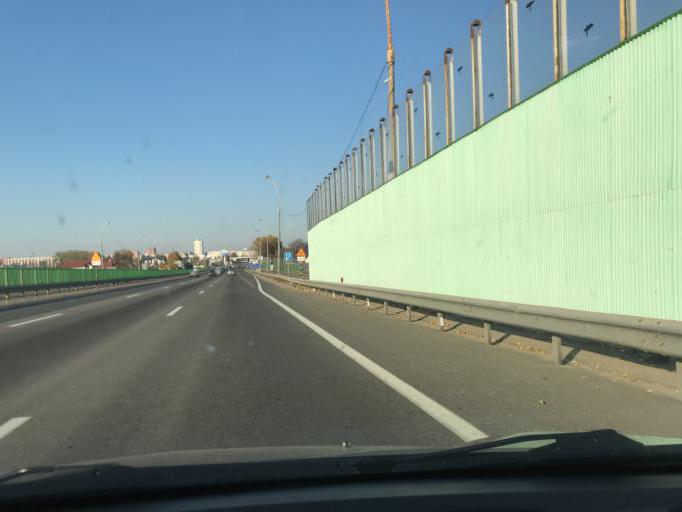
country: BY
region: Minsk
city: Syenitsa
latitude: 53.8285
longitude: 27.5341
